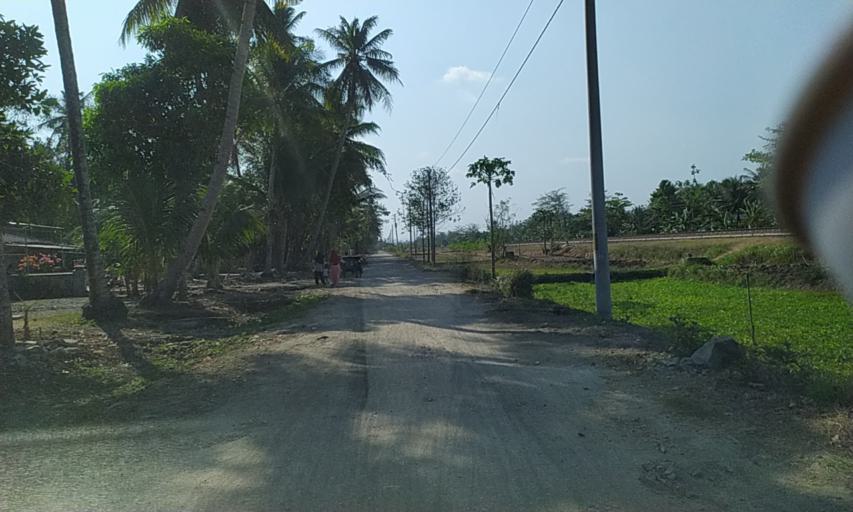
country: ID
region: Central Java
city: Alurbulu
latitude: -7.5047
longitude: 108.8333
